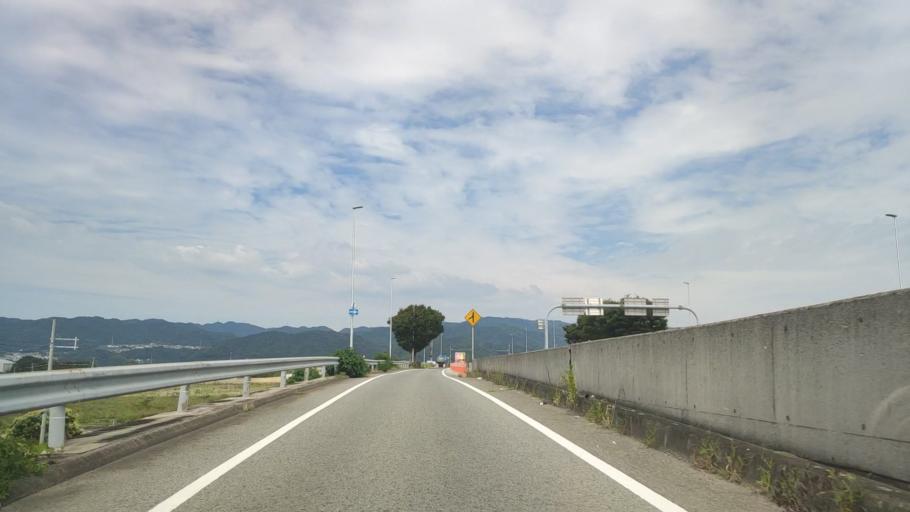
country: JP
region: Wakayama
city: Wakayama-shi
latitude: 34.2465
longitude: 135.2181
